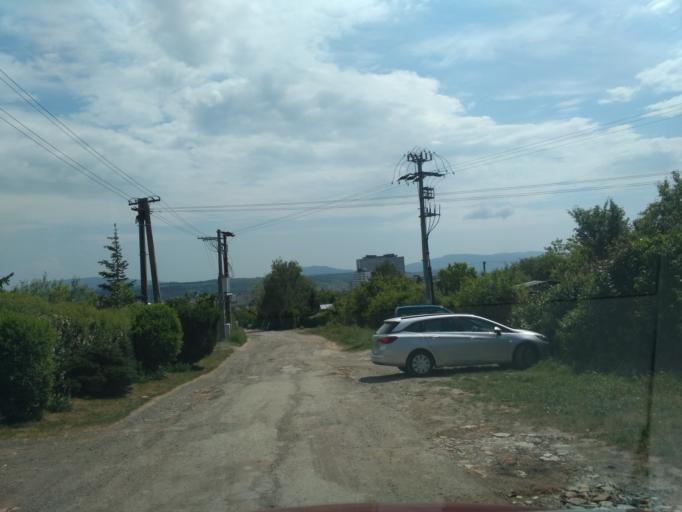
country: SK
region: Kosicky
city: Kosice
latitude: 48.7280
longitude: 21.2263
